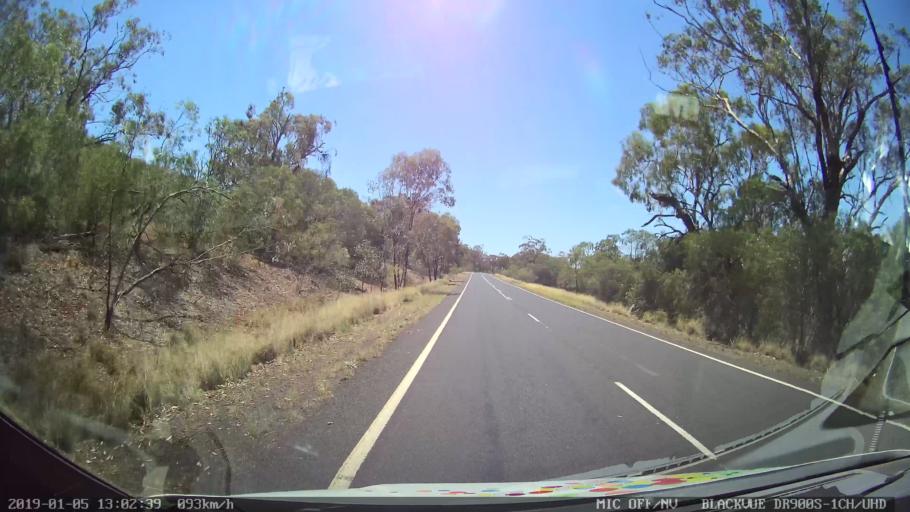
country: AU
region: New South Wales
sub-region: Gunnedah
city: Gunnedah
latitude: -31.1138
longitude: 149.8149
